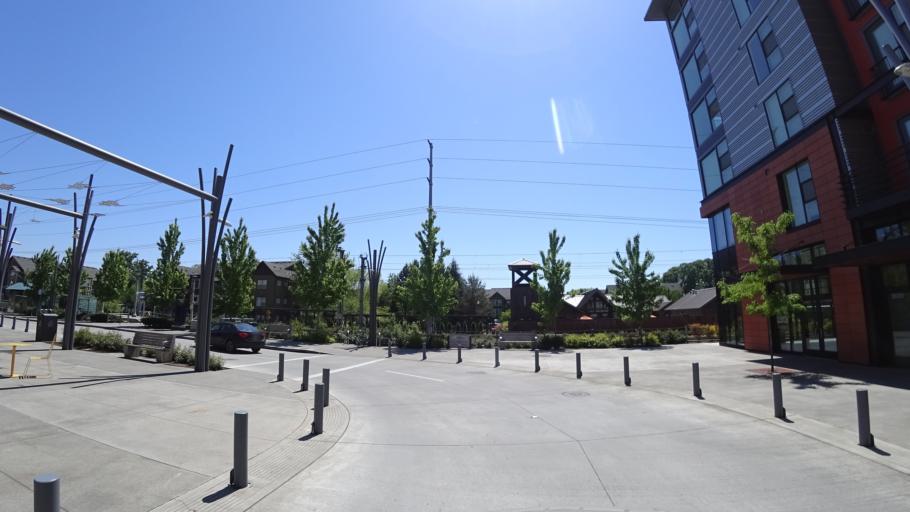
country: US
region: Oregon
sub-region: Washington County
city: Rockcreek
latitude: 45.5306
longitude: -122.9168
